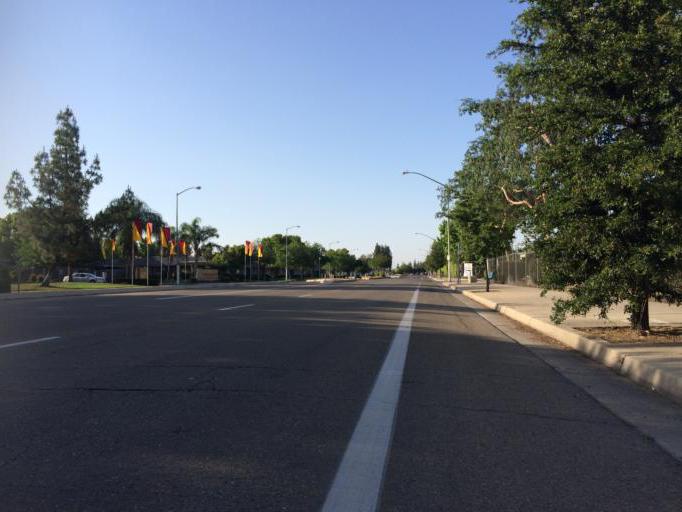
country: US
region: California
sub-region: Fresno County
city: Sunnyside
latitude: 36.7612
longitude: -119.7182
